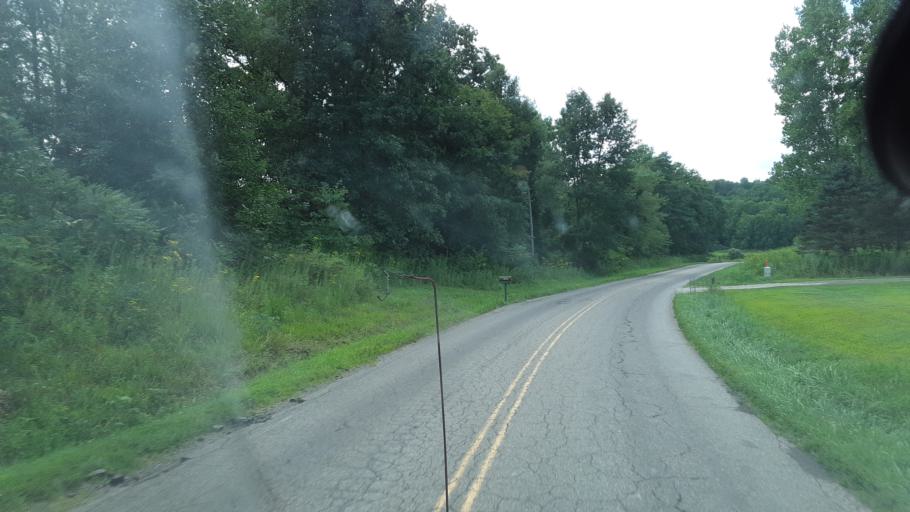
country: US
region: Ohio
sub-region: Knox County
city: Oak Hill
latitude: 40.2693
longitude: -82.2840
